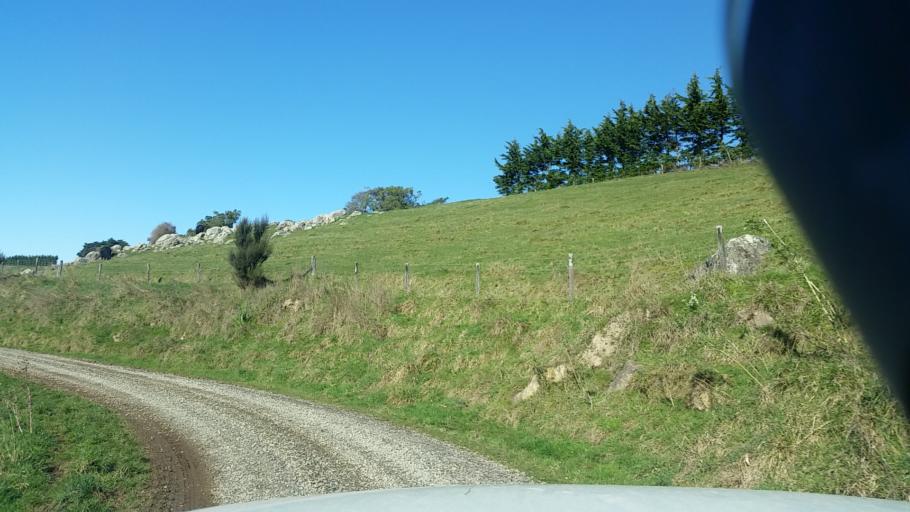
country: NZ
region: Canterbury
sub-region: Christchurch City
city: Christchurch
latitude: -43.6532
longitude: 172.9733
